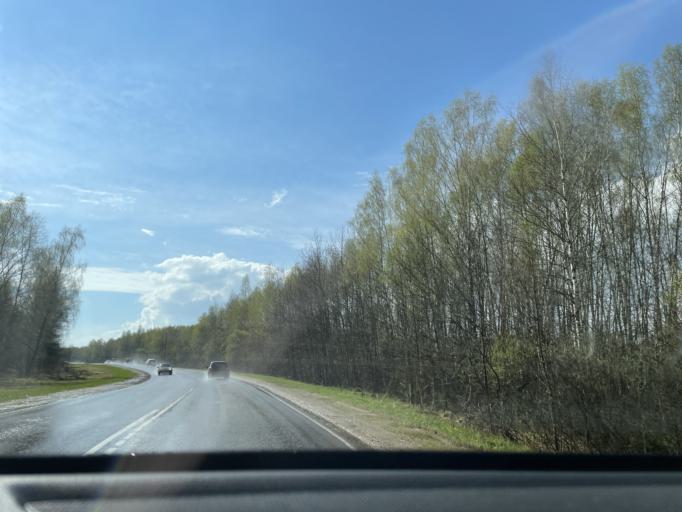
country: RU
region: Tula
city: Aleksin
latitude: 54.5229
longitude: 37.1630
